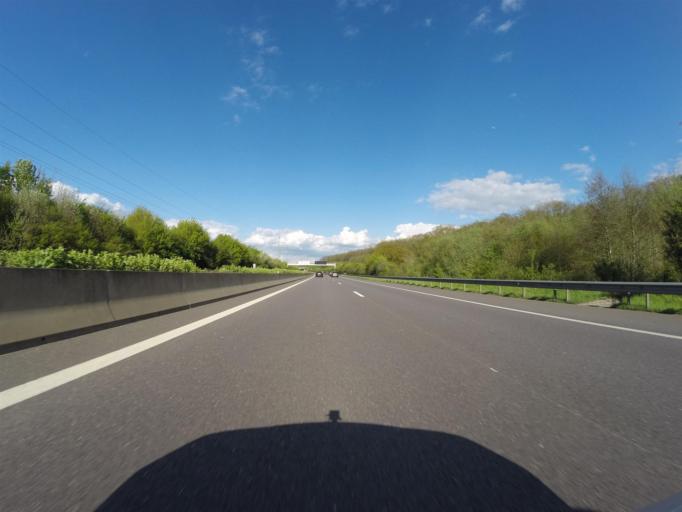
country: LU
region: Luxembourg
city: Aspelt
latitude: 49.5108
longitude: 6.2200
